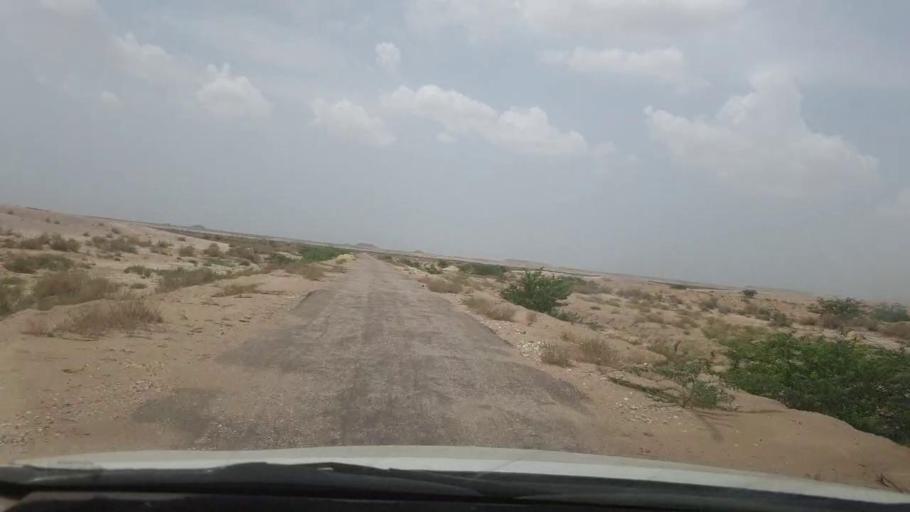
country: PK
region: Sindh
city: Khairpur
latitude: 27.4000
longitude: 68.9707
